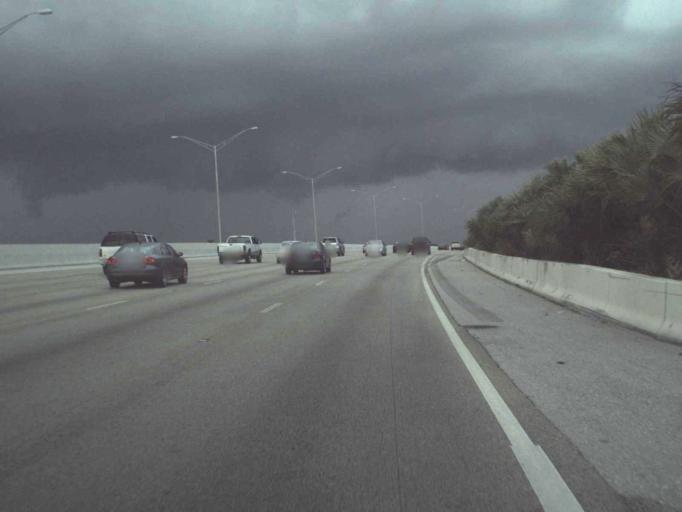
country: US
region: Florida
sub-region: Palm Beach County
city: Schall Circle
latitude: 26.7169
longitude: -80.0874
